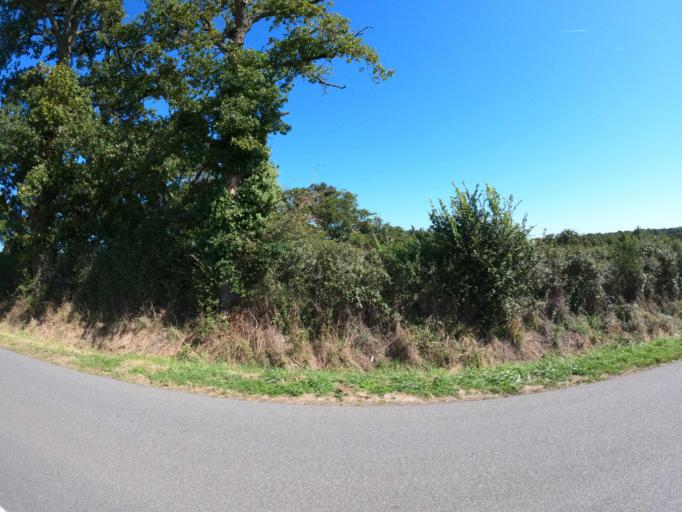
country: FR
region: Limousin
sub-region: Departement de la Haute-Vienne
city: Le Dorat
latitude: 46.2376
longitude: 1.0563
